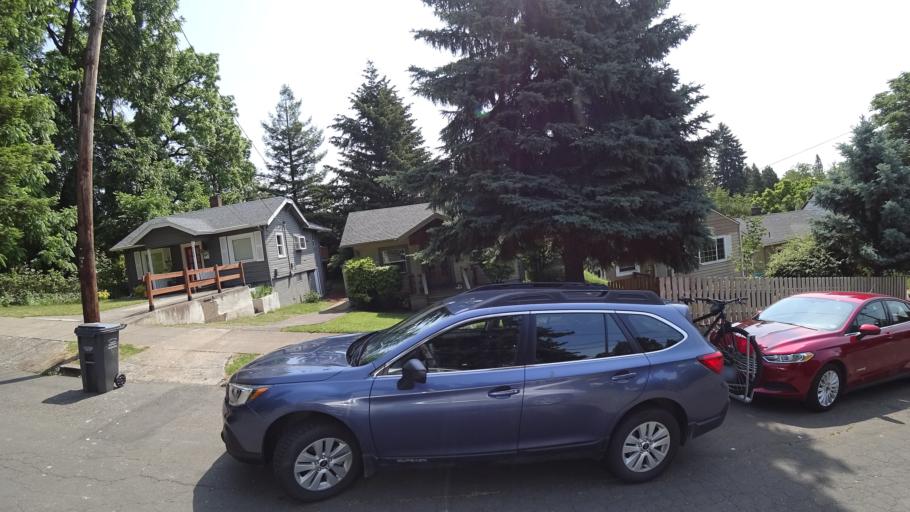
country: US
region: Oregon
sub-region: Multnomah County
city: Lents
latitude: 45.5071
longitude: -122.5908
